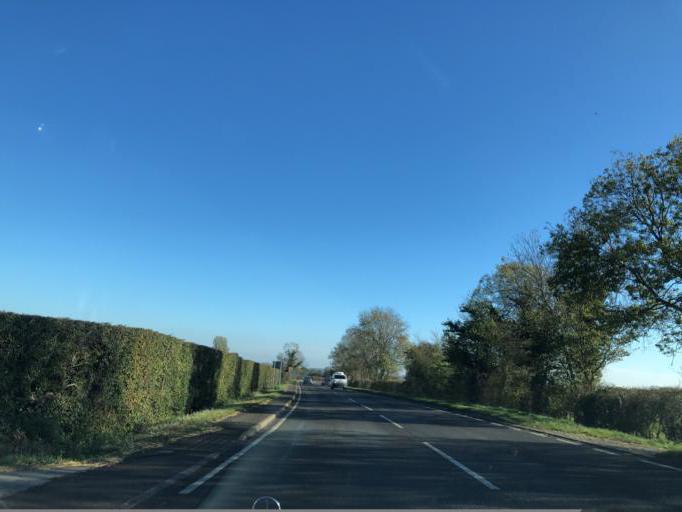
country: GB
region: England
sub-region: Warwickshire
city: Harbury
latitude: 52.2548
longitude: -1.4388
